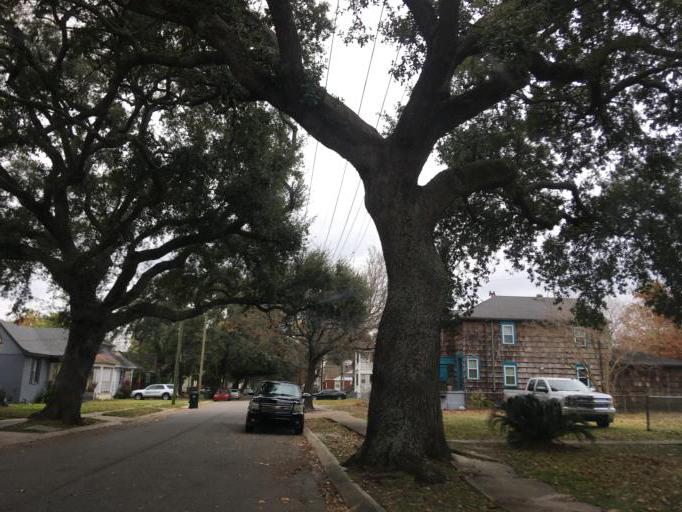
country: US
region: Louisiana
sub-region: Orleans Parish
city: New Orleans
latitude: 29.9917
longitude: -90.0623
